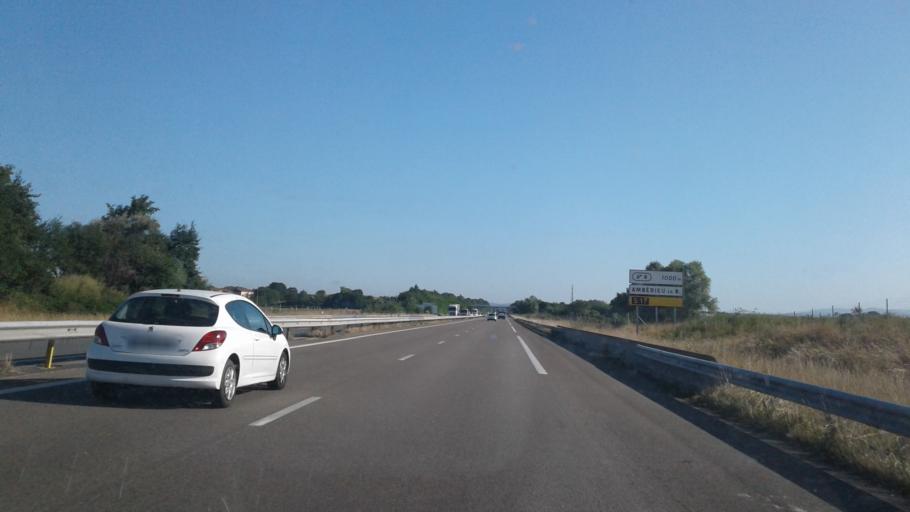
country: FR
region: Rhone-Alpes
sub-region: Departement de l'Ain
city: Chateau-Gaillard
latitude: 45.9669
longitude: 5.3077
